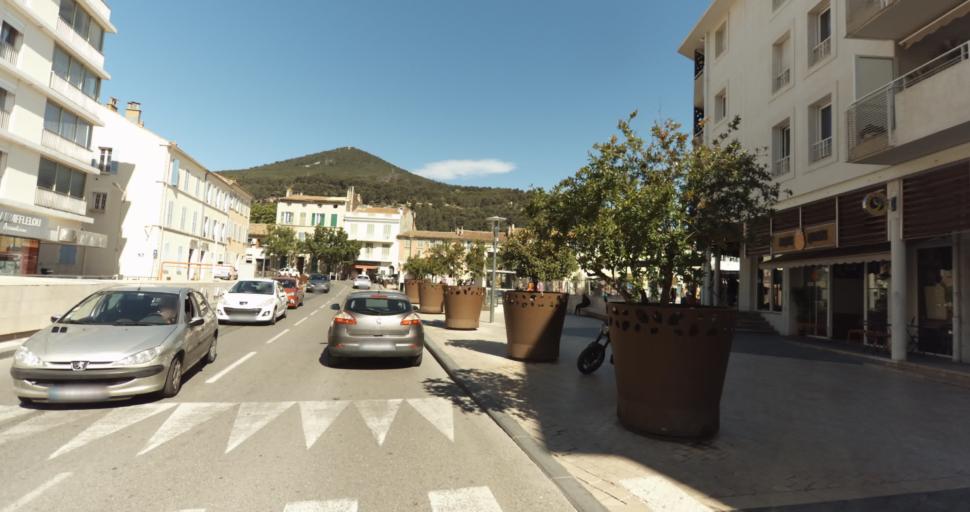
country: FR
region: Provence-Alpes-Cote d'Azur
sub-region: Departement du Var
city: La Valette-du-Var
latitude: 43.1367
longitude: 5.9813
